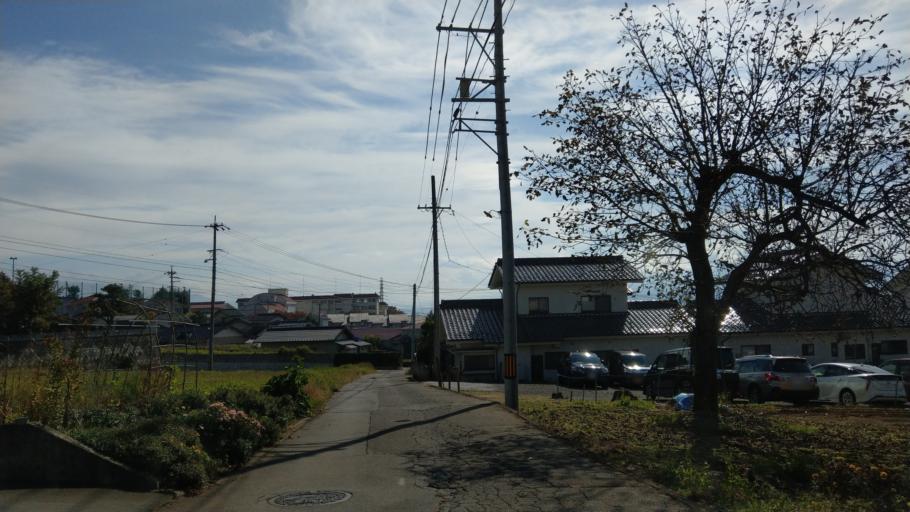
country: JP
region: Nagano
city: Komoro
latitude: 36.3336
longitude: 138.4427
